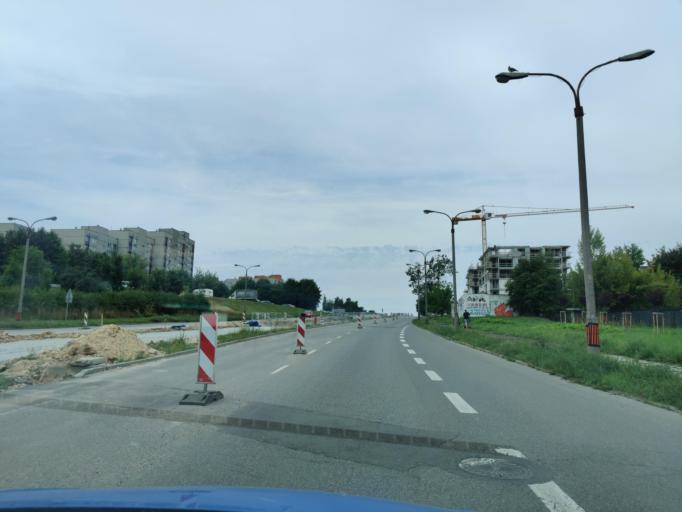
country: PL
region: Silesian Voivodeship
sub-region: Dabrowa Gornicza
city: Dabrowa Gornicza
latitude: 50.2825
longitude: 19.1907
